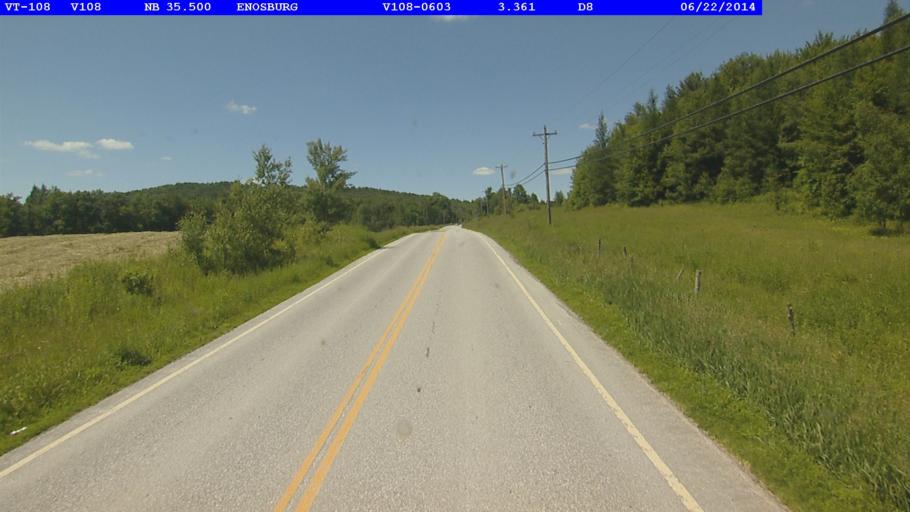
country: US
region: Vermont
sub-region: Franklin County
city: Enosburg Falls
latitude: 44.8844
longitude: -72.8008
